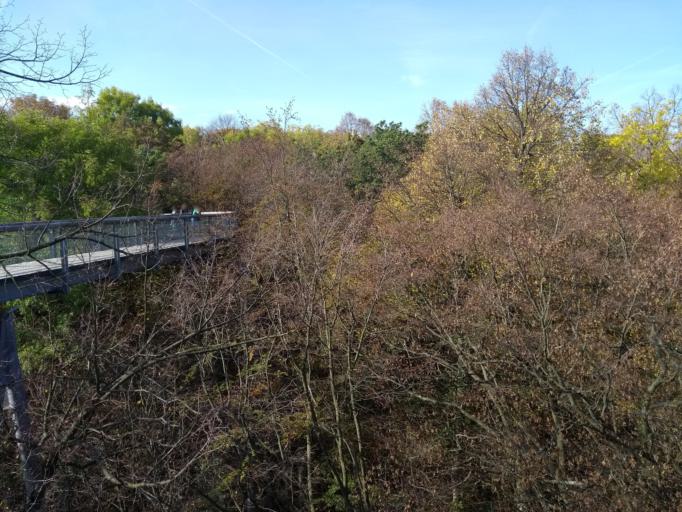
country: DE
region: Thuringia
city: Weberstedt
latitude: 51.0841
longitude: 10.5106
